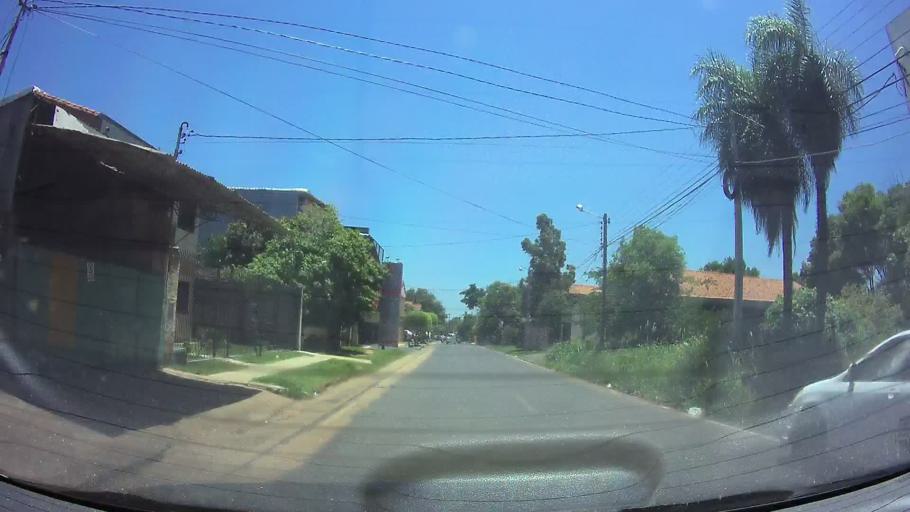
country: PY
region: Central
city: San Lorenzo
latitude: -25.2713
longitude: -57.5074
